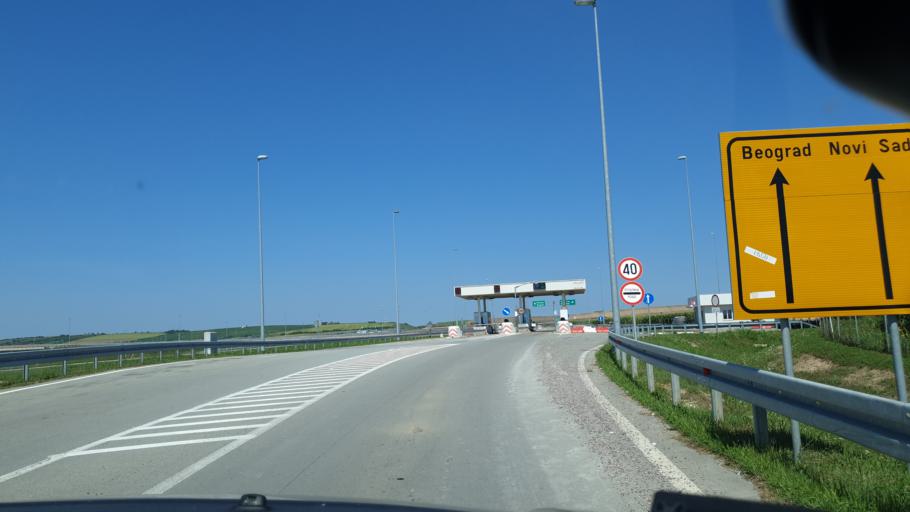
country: RS
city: Beska
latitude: 45.1342
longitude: 20.0904
